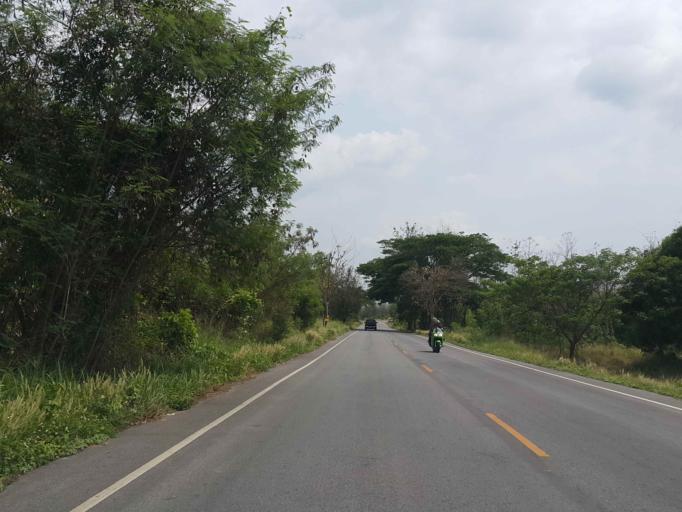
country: TH
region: Lampang
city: Thoen
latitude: 17.5059
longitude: 99.3507
